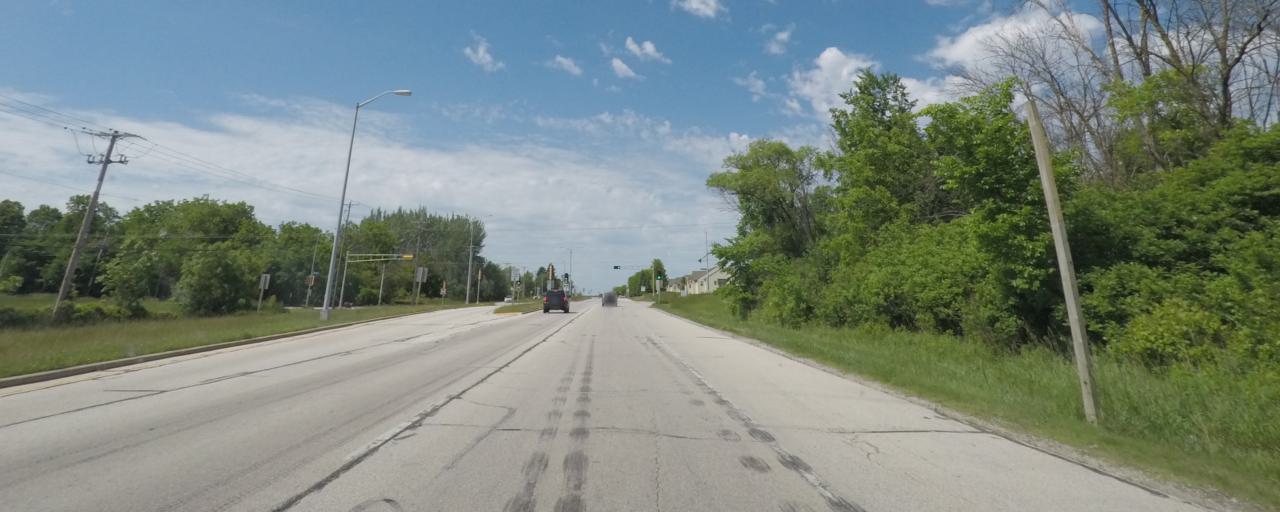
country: US
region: Wisconsin
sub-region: Milwaukee County
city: Greendale
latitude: 42.8863
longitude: -87.9507
